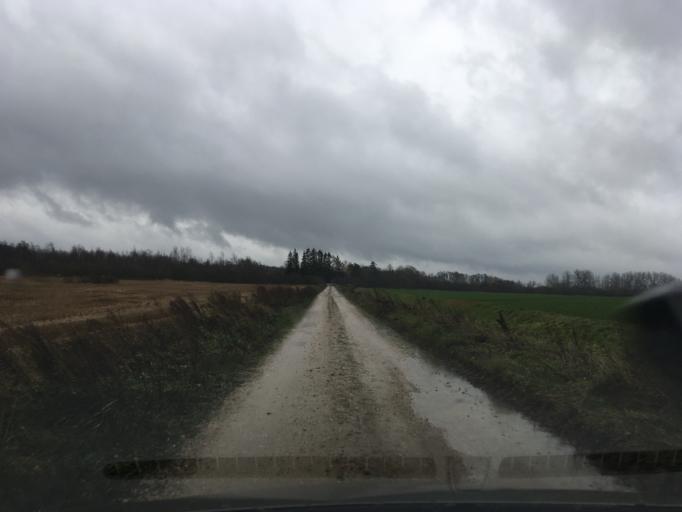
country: EE
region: Laeaene
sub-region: Lihula vald
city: Lihula
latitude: 58.7031
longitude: 23.8550
